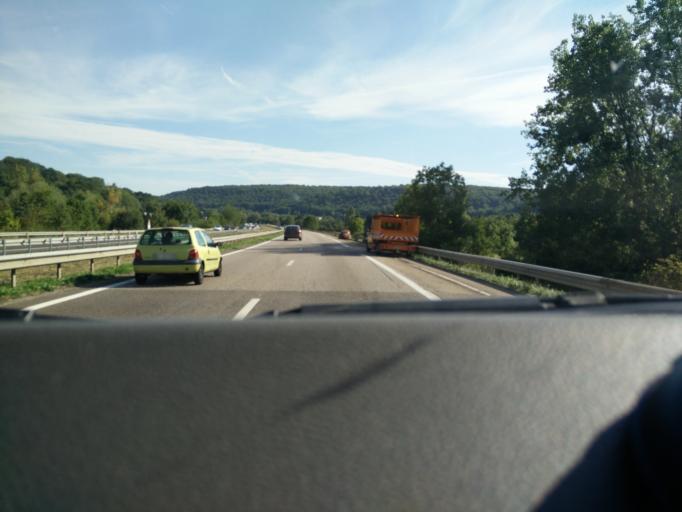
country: FR
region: Lorraine
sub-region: Departement de Meurthe-et-Moselle
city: Marbache
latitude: 48.8014
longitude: 6.1134
